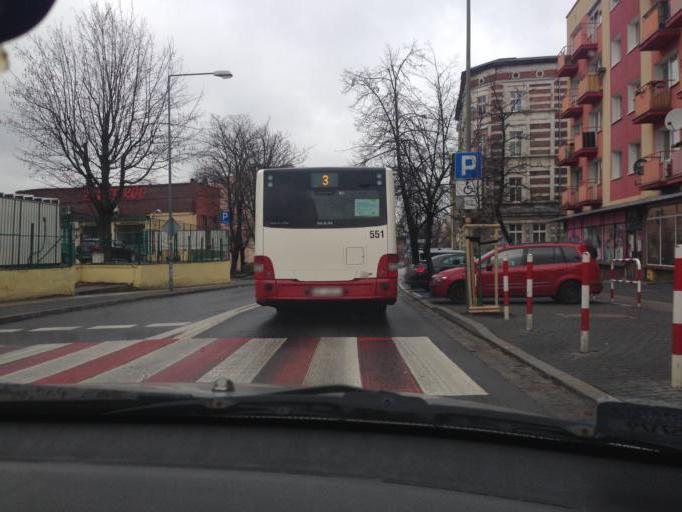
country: PL
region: Opole Voivodeship
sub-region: Powiat opolski
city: Opole
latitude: 50.6713
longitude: 17.9232
